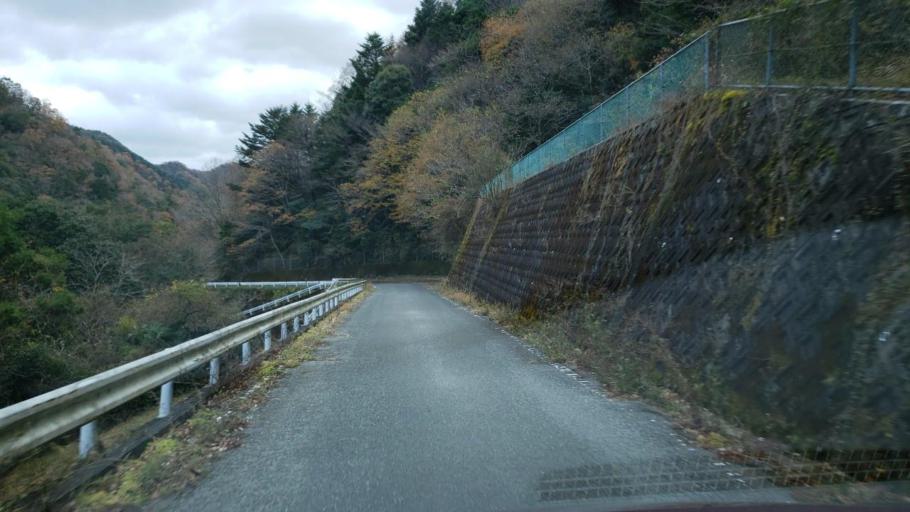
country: JP
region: Tokushima
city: Wakimachi
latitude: 34.1471
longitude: 134.2278
